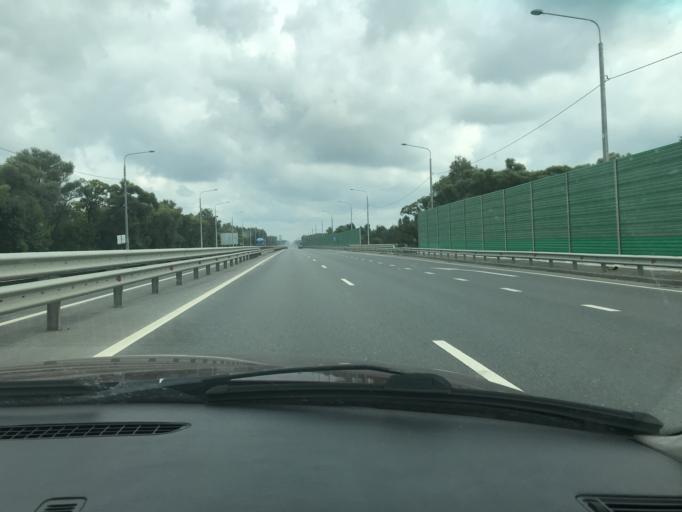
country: RU
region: Kaluga
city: Pyatovskiy
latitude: 54.7340
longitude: 36.1809
